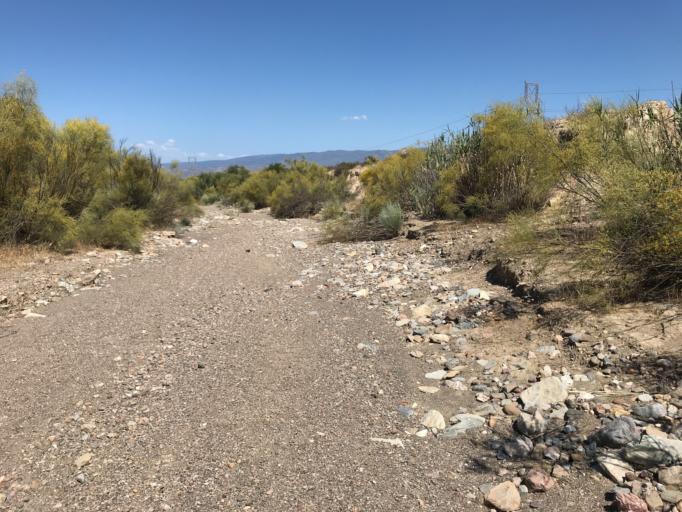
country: ES
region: Andalusia
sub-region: Provincia de Almeria
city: Turrillas
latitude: 37.0690
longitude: -2.2911
